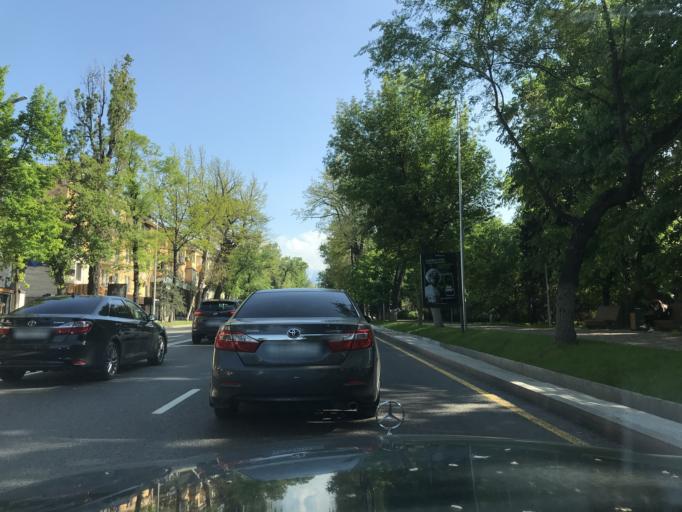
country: KZ
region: Almaty Qalasy
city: Almaty
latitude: 43.2495
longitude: 76.9473
